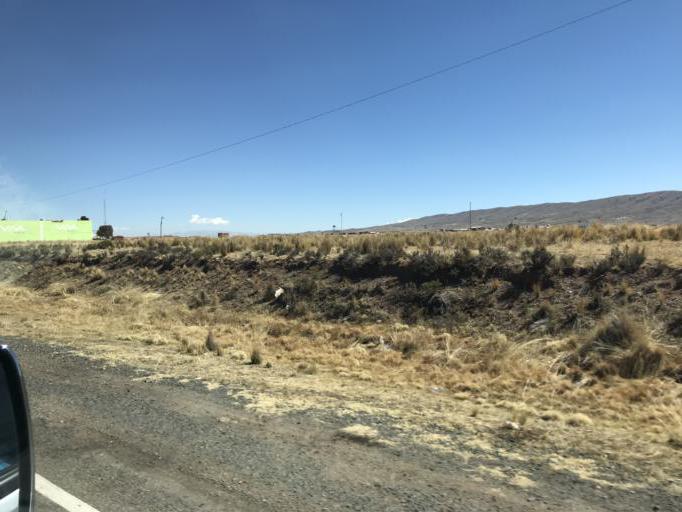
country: BO
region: La Paz
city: Tiahuanaco
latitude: -16.5706
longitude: -68.6698
